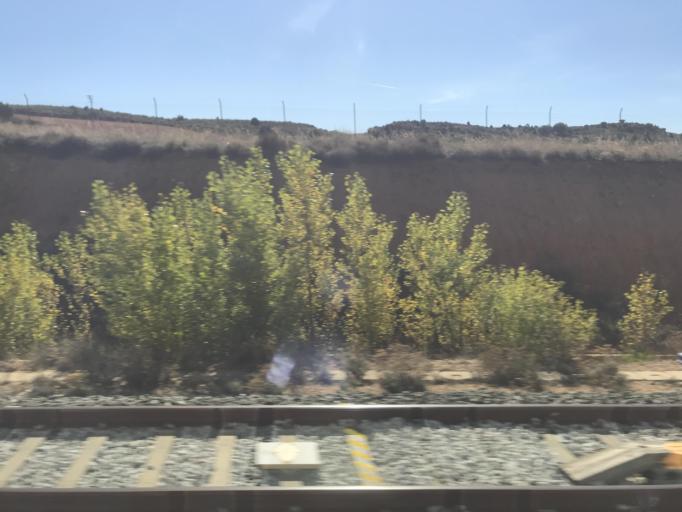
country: ES
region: Aragon
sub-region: Provincia de Zaragoza
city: Cabolafuente
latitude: 41.2268
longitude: -2.0673
